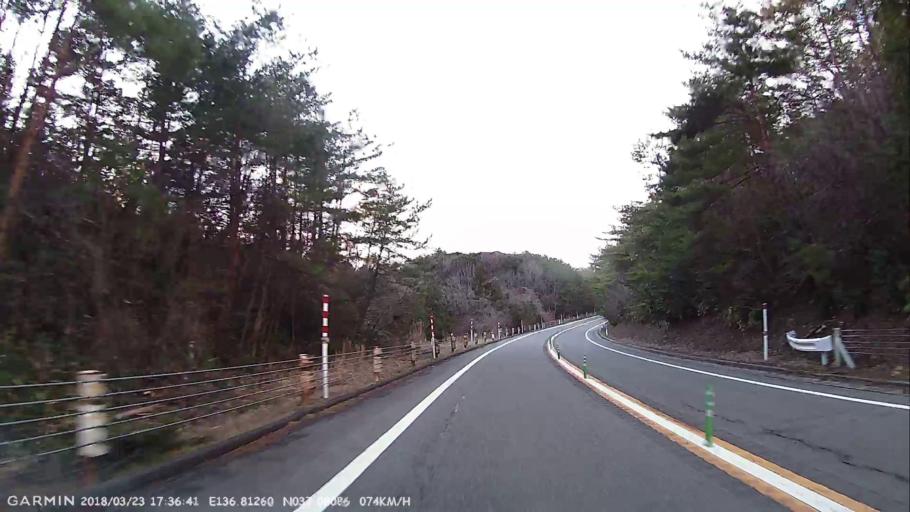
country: JP
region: Ishikawa
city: Nanao
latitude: 37.0809
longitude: 136.8125
